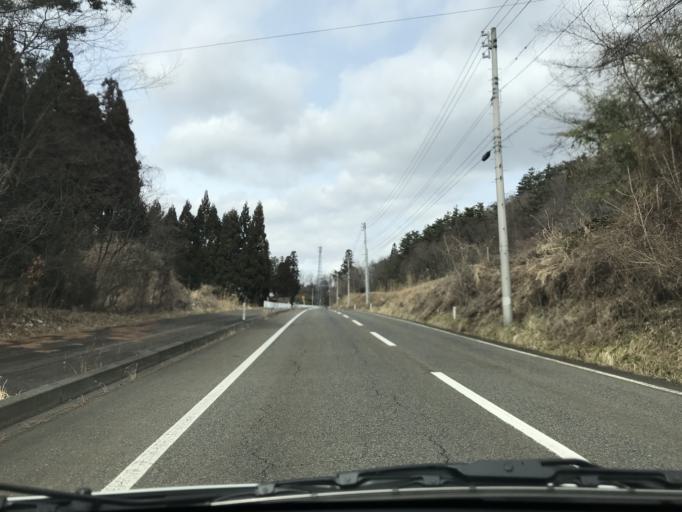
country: JP
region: Iwate
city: Tono
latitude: 39.2938
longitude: 141.3303
